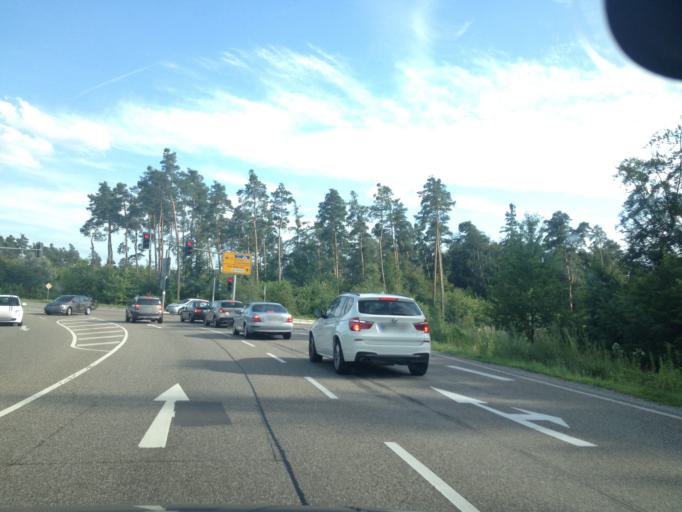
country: DE
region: Baden-Wuerttemberg
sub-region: Karlsruhe Region
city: Graben-Neudorf
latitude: 49.1560
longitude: 8.5079
